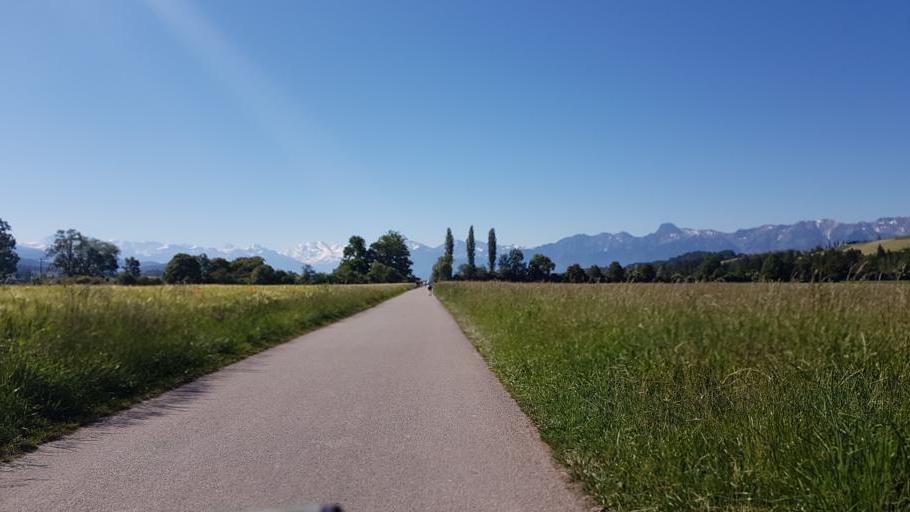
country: CH
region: Bern
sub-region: Bern-Mittelland District
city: Munsingen
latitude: 46.8606
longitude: 7.5590
